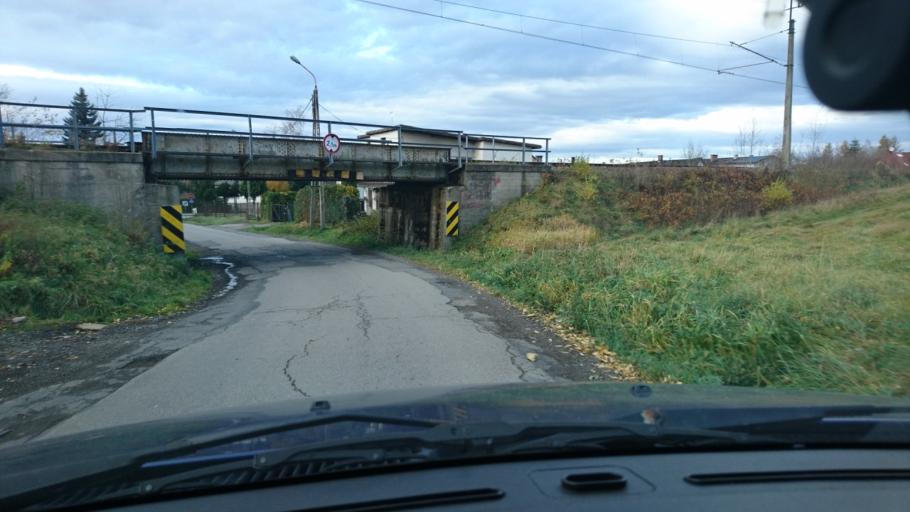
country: PL
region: Silesian Voivodeship
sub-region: Powiat bielski
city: Kozy
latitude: 49.8412
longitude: 19.1163
